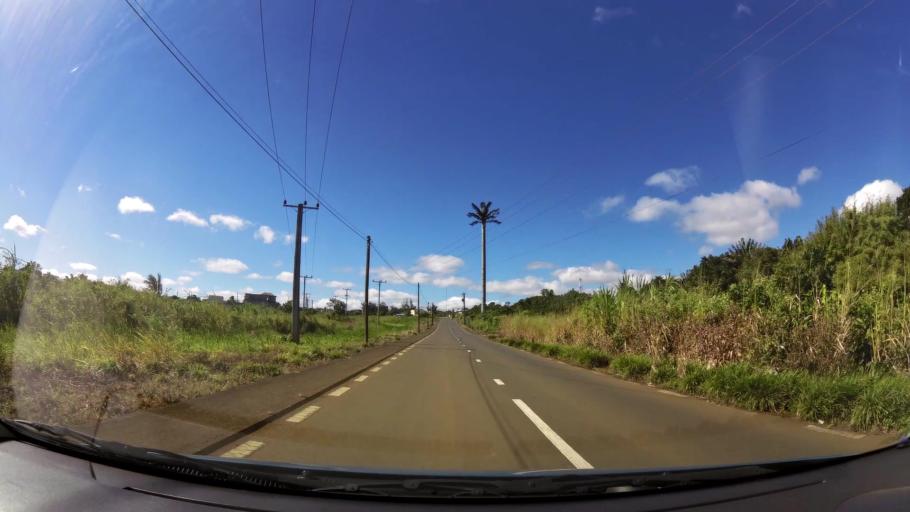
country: MU
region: Plaines Wilhems
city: Curepipe
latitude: -20.3413
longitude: 57.4887
